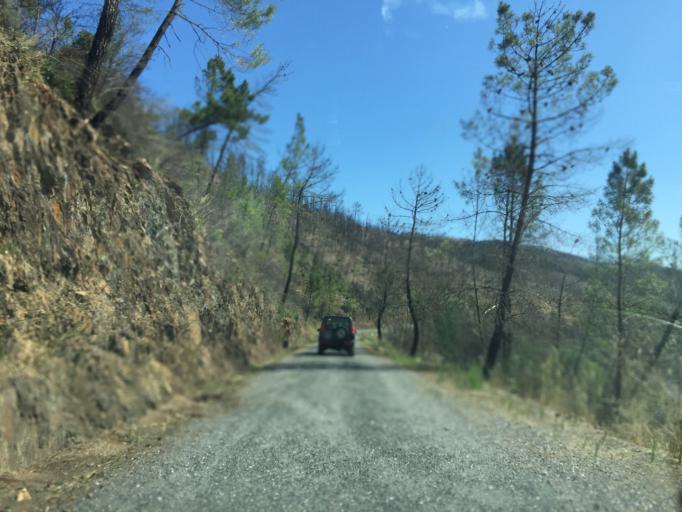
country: PT
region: Coimbra
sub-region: Pampilhosa da Serra
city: Pampilhosa da Serra
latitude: 40.0182
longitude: -7.8491
